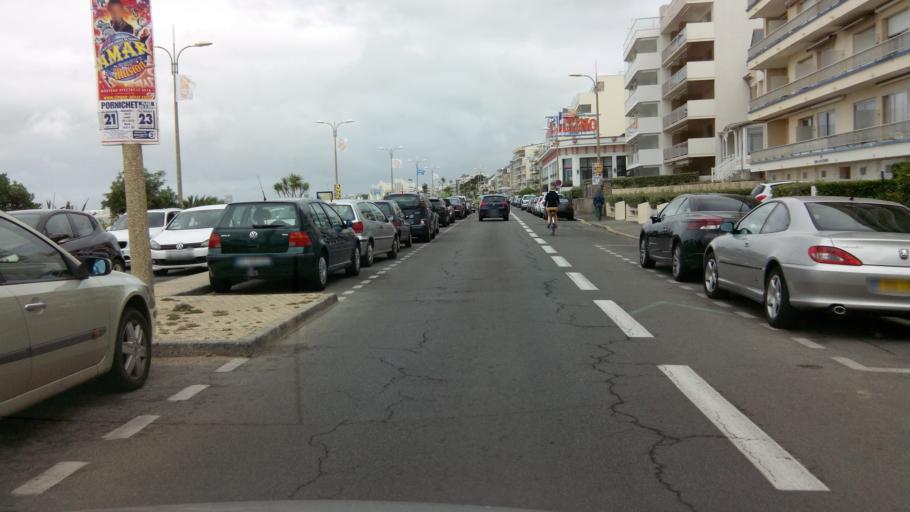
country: FR
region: Pays de la Loire
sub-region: Departement de la Loire-Atlantique
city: Pornichet
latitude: 47.2661
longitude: -2.3460
